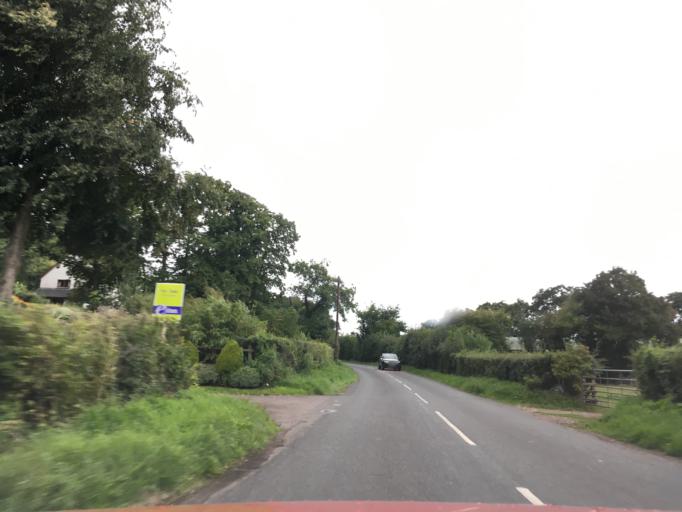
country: GB
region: Wales
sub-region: Monmouthshire
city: Llangybi
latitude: 51.6681
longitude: -2.8825
